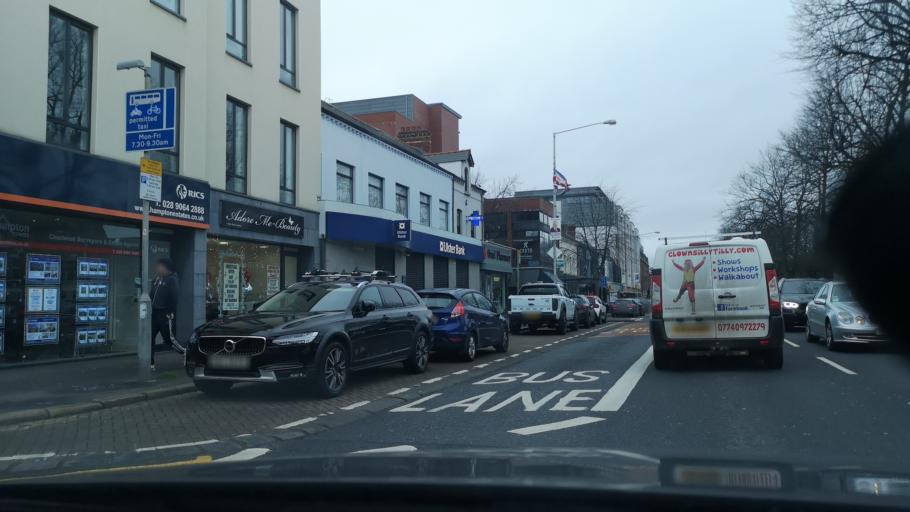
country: GB
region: Northern Ireland
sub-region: City of Belfast
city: Belfast
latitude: 54.5781
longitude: -5.9190
